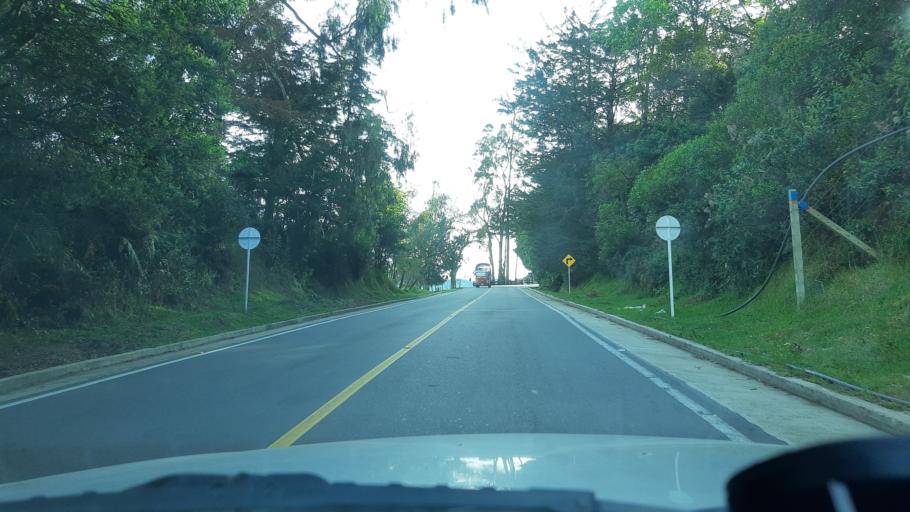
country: CO
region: Cundinamarca
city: Choconta
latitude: 5.0979
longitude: -73.6616
